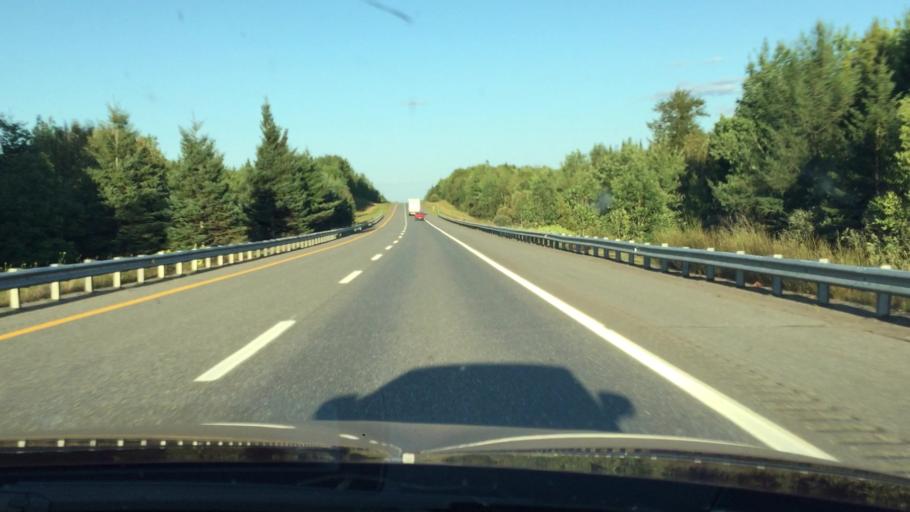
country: US
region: Maine
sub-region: Aroostook County
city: Hodgdon
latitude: 46.1398
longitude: -68.0128
